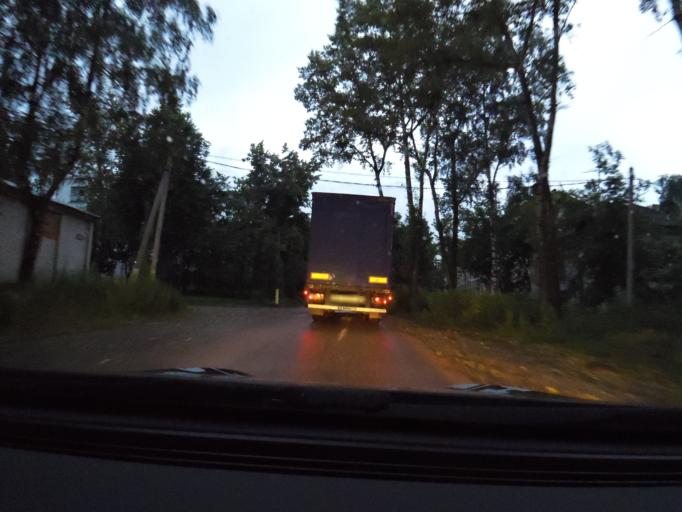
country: RU
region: Vladimir
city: Aleksandrov
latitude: 56.4009
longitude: 38.7287
